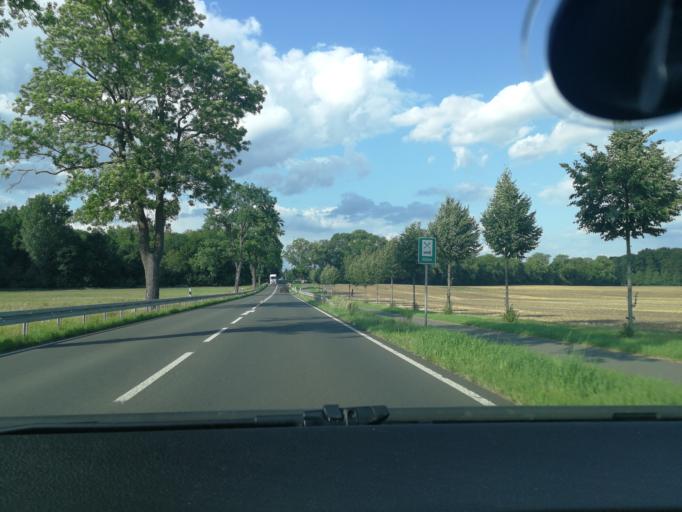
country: DE
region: Brandenburg
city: Pritzwalk
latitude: 53.1684
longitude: 12.1857
